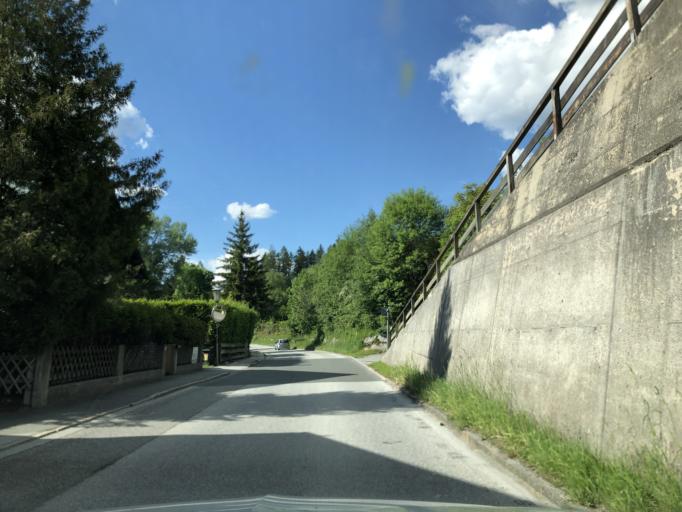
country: AT
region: Salzburg
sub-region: Politischer Bezirk Zell am See
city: Bruck an der Grossglocknerstrasse
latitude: 47.3107
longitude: 12.8167
